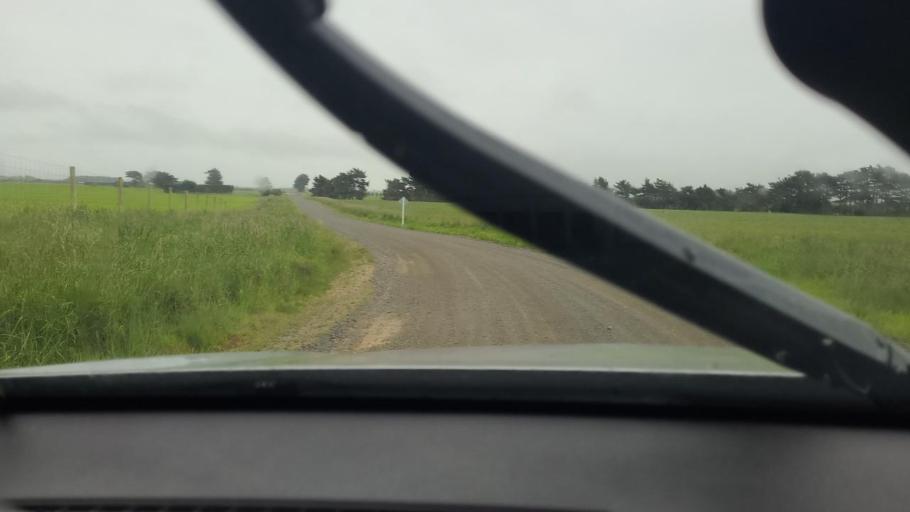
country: NZ
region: Southland
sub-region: Southland District
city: Riverton
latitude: -46.3153
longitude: 168.1834
